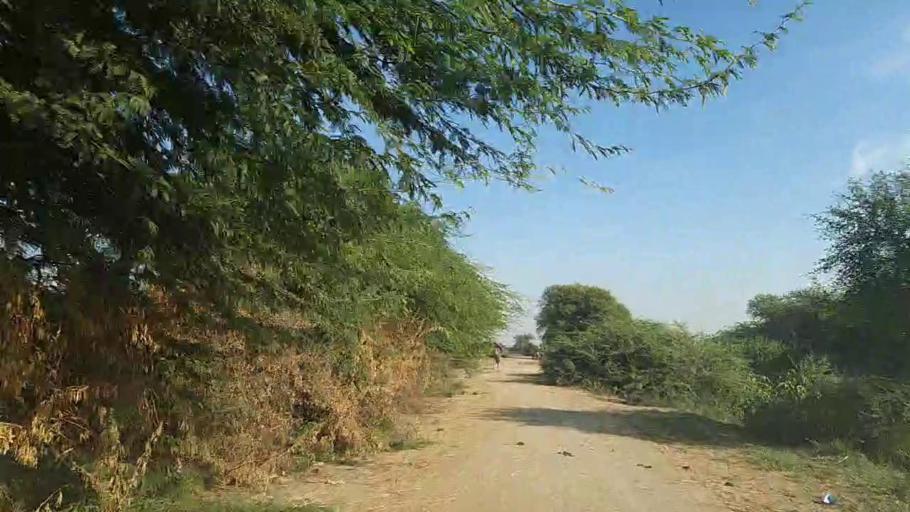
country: PK
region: Sindh
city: Bulri
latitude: 24.7775
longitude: 68.3585
